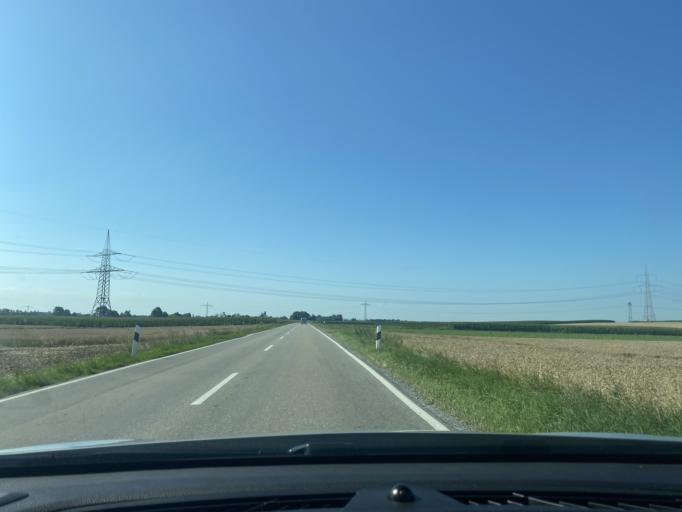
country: DE
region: Bavaria
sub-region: Upper Bavaria
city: Eitting
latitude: 48.3451
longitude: 11.8971
